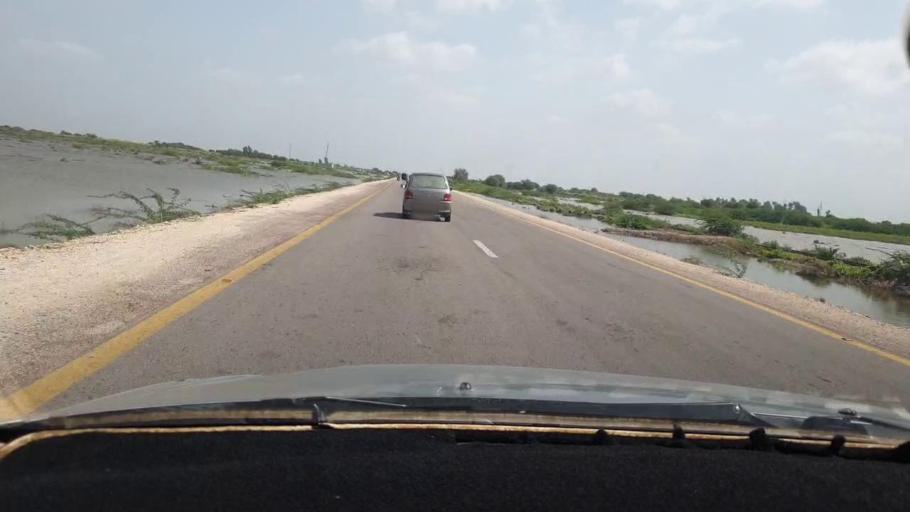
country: PK
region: Sindh
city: Digri
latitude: 25.1244
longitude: 69.1462
